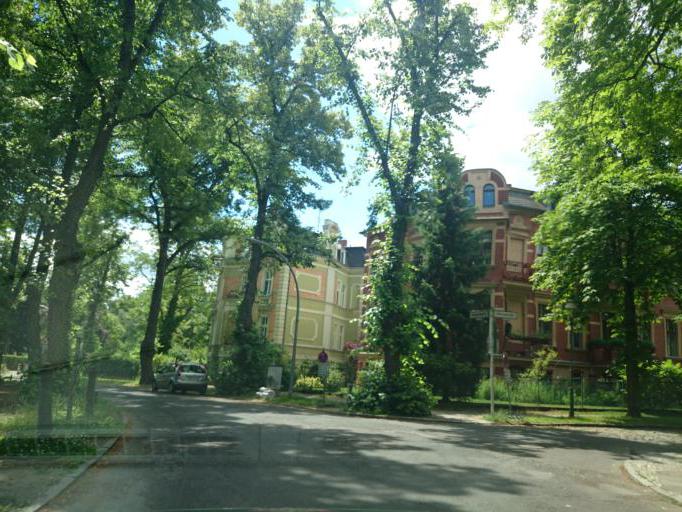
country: DE
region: Berlin
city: Lichterfelde
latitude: 52.4430
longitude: 13.3068
